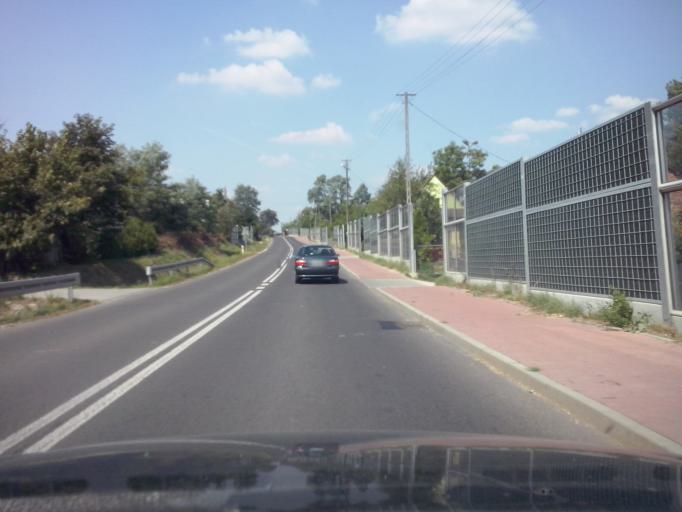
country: PL
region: Swietokrzyskie
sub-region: Powiat buski
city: Gnojno
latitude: 50.5920
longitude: 20.8860
